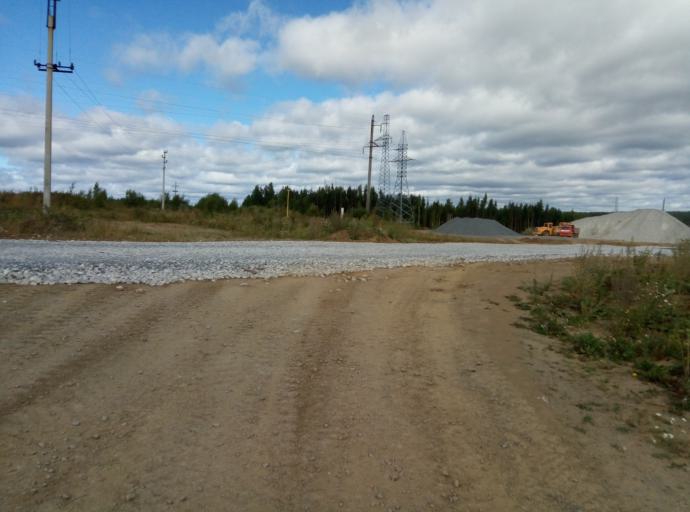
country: RU
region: Sverdlovsk
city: Karpinsk
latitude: 59.6226
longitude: 59.5924
